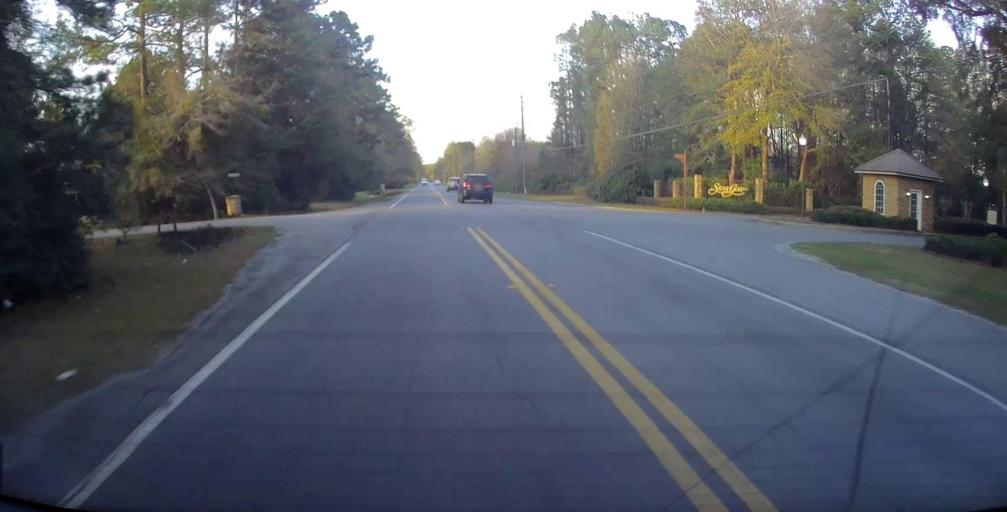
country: US
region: Georgia
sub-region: Chatham County
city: Bloomingdale
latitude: 32.1550
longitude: -81.3876
